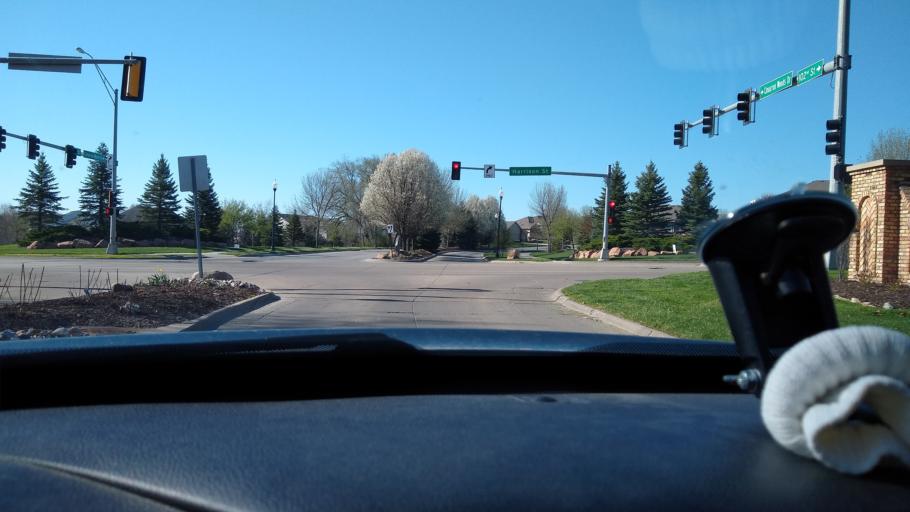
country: US
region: Nebraska
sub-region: Douglas County
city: Ralston
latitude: 41.1911
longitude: -96.0718
